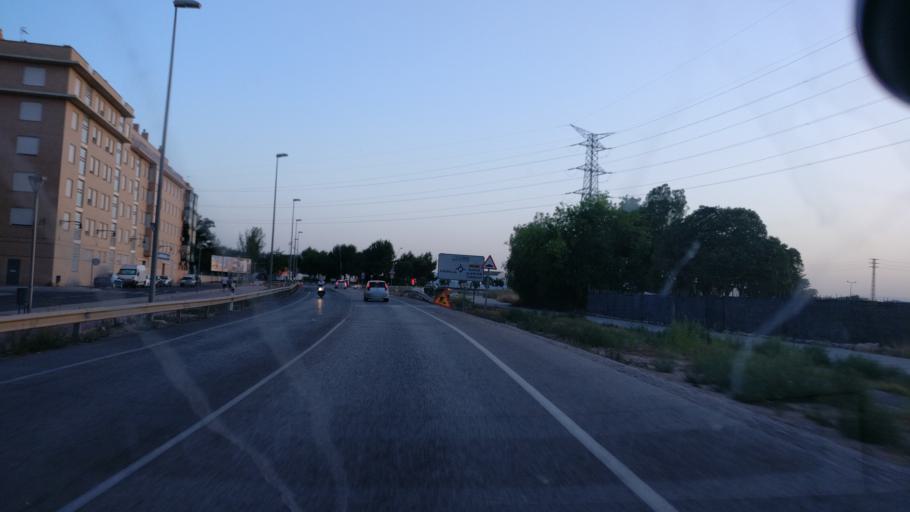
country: ES
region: Valencia
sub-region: Provincia de Valencia
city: Xirivella
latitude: 39.4658
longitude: -0.4380
